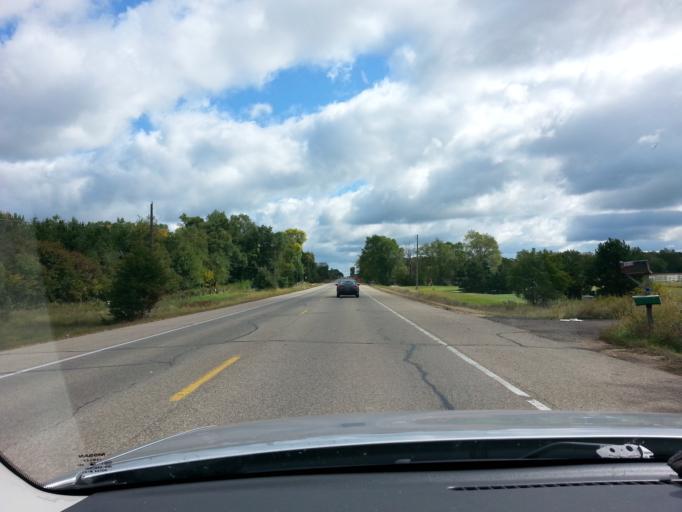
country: US
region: Minnesota
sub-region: Washington County
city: Lake Elmo
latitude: 44.9635
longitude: -92.8928
